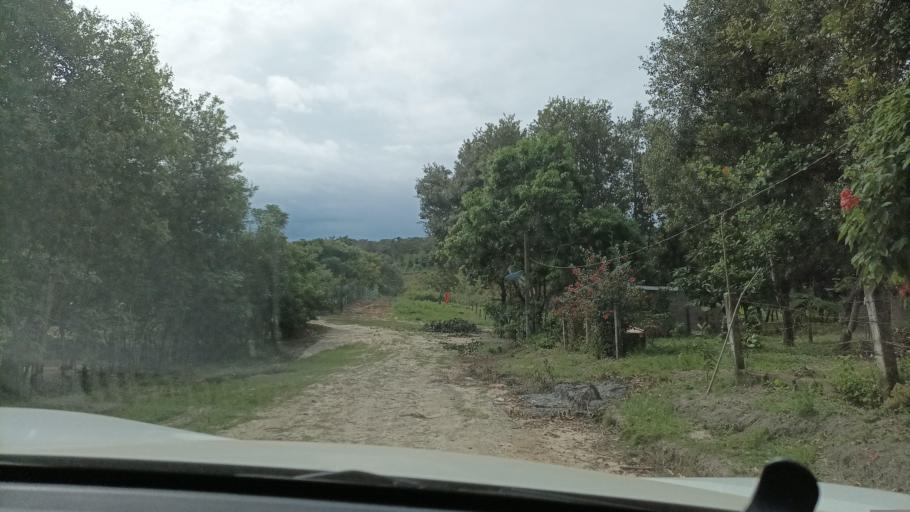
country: MX
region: Veracruz
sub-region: Cosoleacaque
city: Coacotla
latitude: 17.9463
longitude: -94.7109
